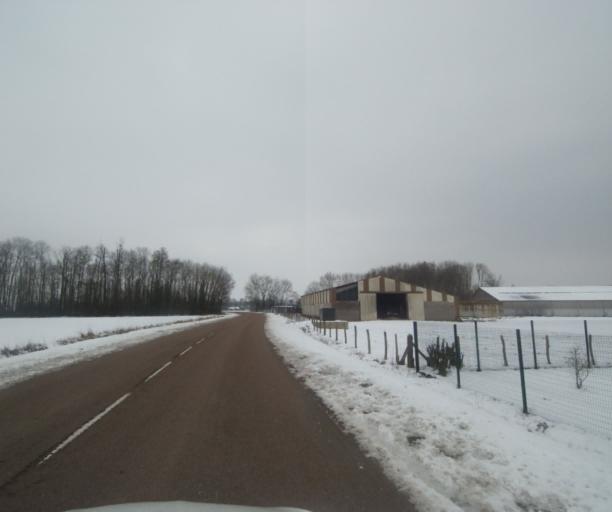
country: FR
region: Champagne-Ardenne
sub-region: Departement de la Haute-Marne
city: Villiers-en-Lieu
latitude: 48.5945
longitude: 4.8469
